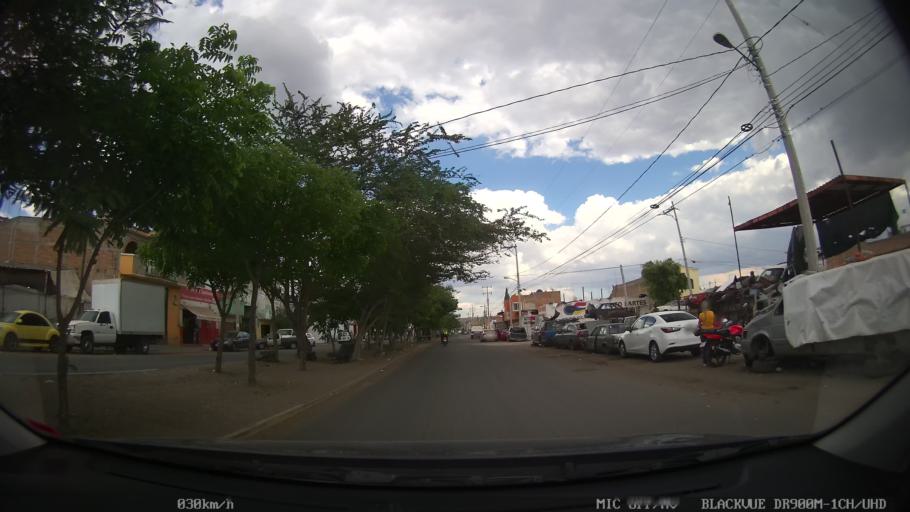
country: MX
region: Jalisco
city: Tlaquepaque
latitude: 20.6693
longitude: -103.2556
